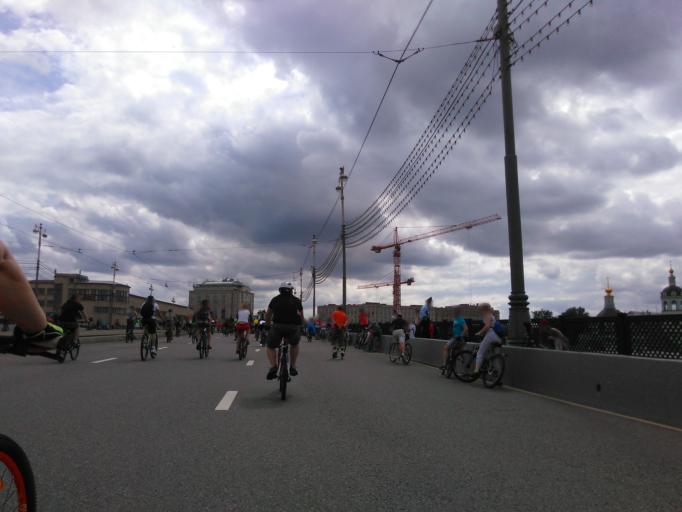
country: RU
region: Moscow
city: Zamoskvorech'ye
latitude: 55.7478
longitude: 37.6394
